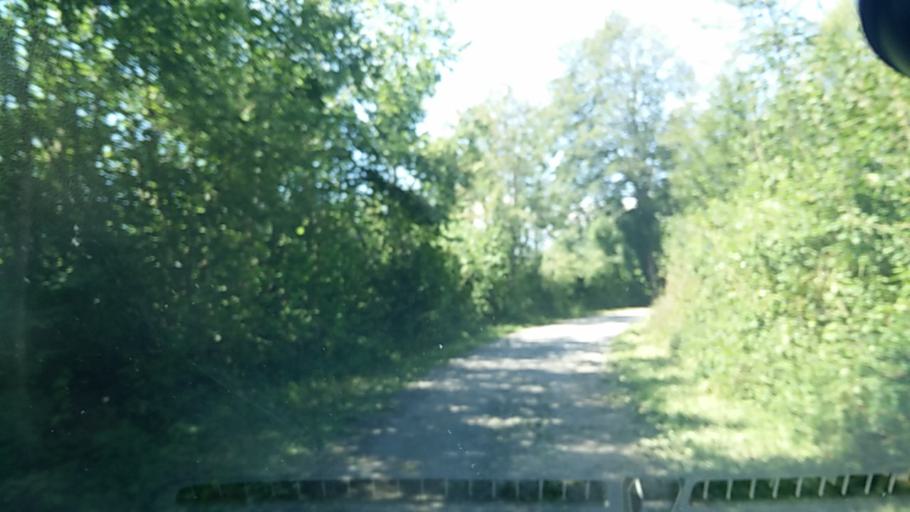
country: AT
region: Carinthia
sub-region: Politischer Bezirk Volkermarkt
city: Sittersdorf
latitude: 46.5401
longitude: 14.5917
